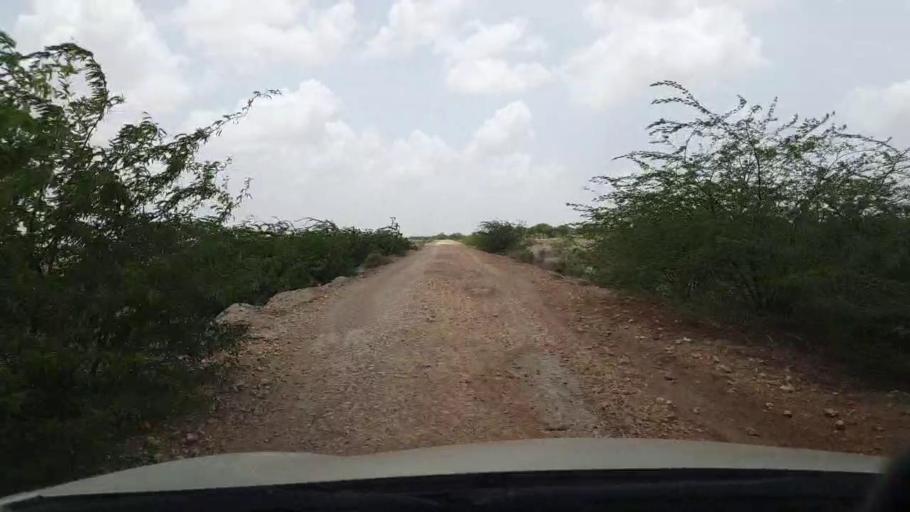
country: PK
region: Sindh
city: Kadhan
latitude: 24.3685
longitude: 68.9272
